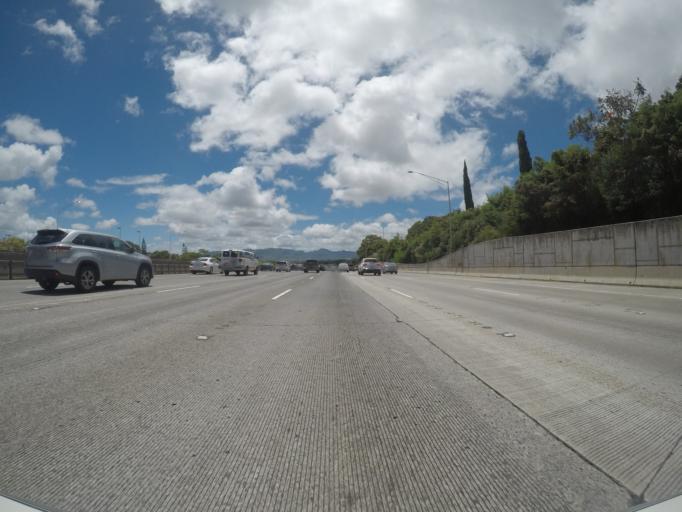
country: US
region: Hawaii
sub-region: Honolulu County
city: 'Aiea
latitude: 21.3893
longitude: -157.9425
